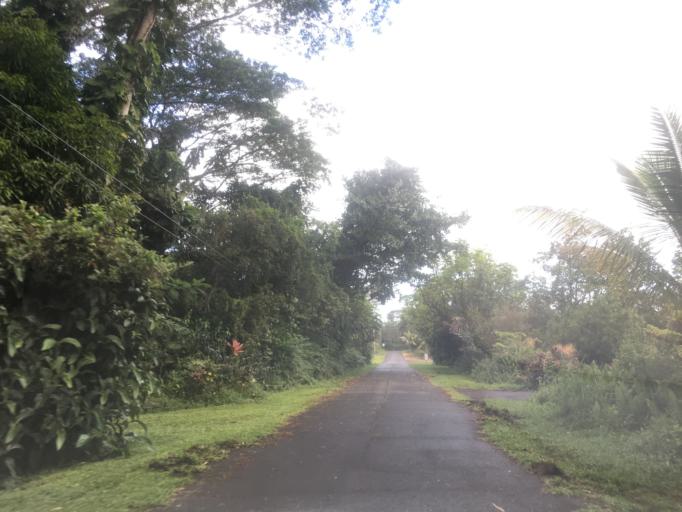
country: US
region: Hawaii
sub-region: Hawaii County
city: Leilani Estates
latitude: 19.4857
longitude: -154.9246
